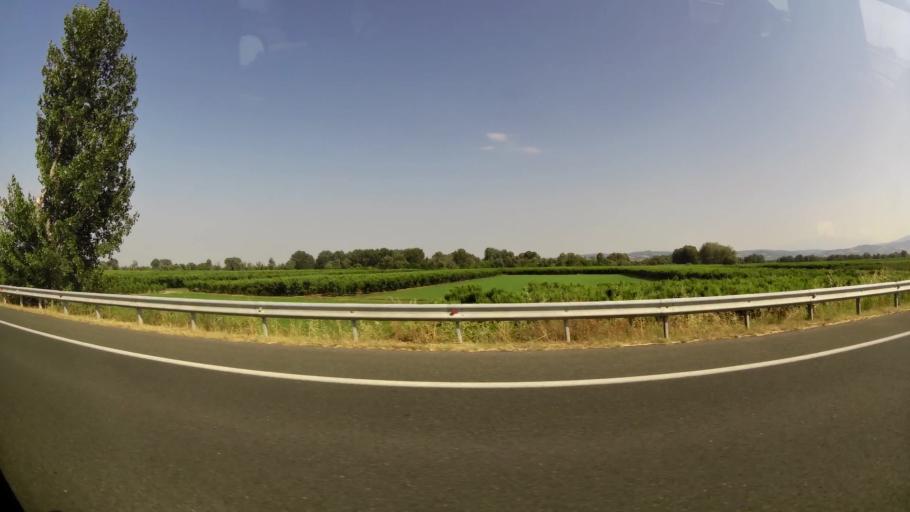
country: GR
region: Central Macedonia
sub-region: Nomos Imathias
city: Loutros
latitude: 40.5810
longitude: 22.4084
